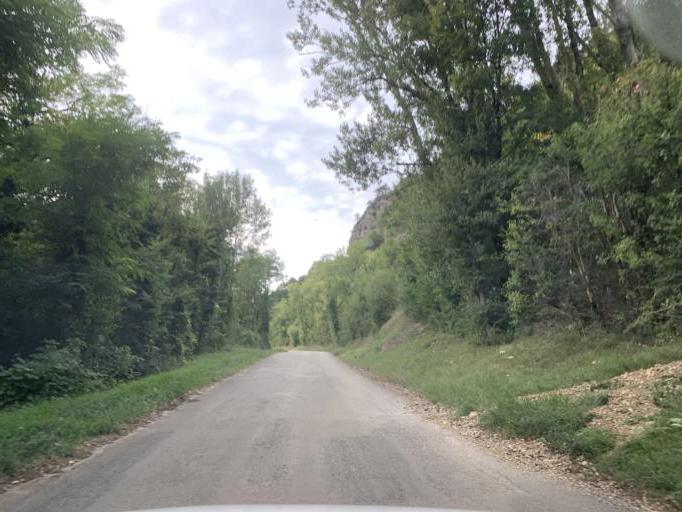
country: FR
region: Rhone-Alpes
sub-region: Departement de l'Ain
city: Vaux-en-Bugey
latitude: 45.9325
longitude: 5.3852
